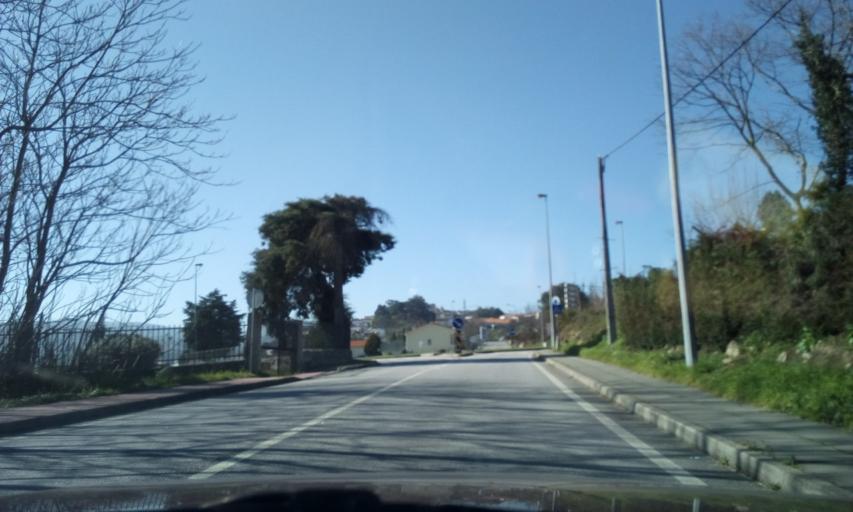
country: PT
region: Guarda
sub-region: Celorico da Beira
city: Celorico da Beira
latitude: 40.6462
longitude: -7.3840
